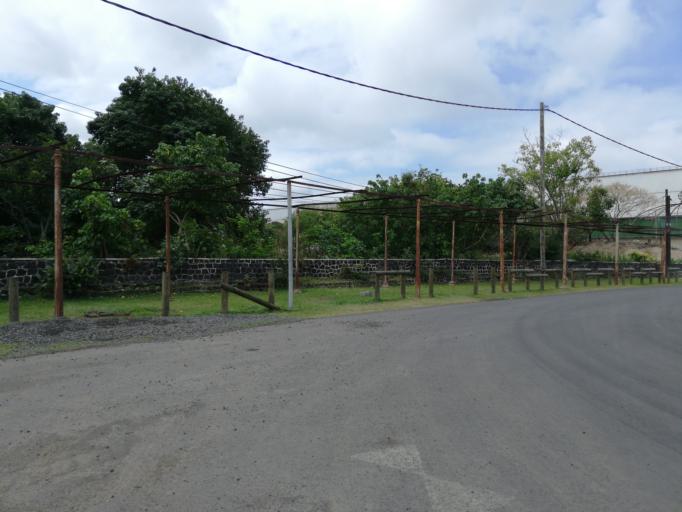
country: MU
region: Port Louis
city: Port Louis
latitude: -20.1572
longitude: 57.4865
